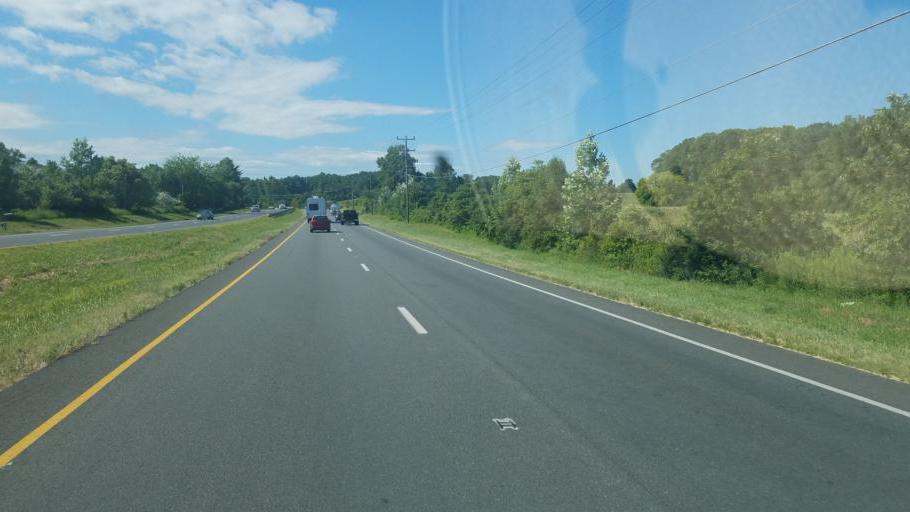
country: US
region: Virginia
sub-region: Fauquier County
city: Warrenton
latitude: 38.6483
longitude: -77.8035
